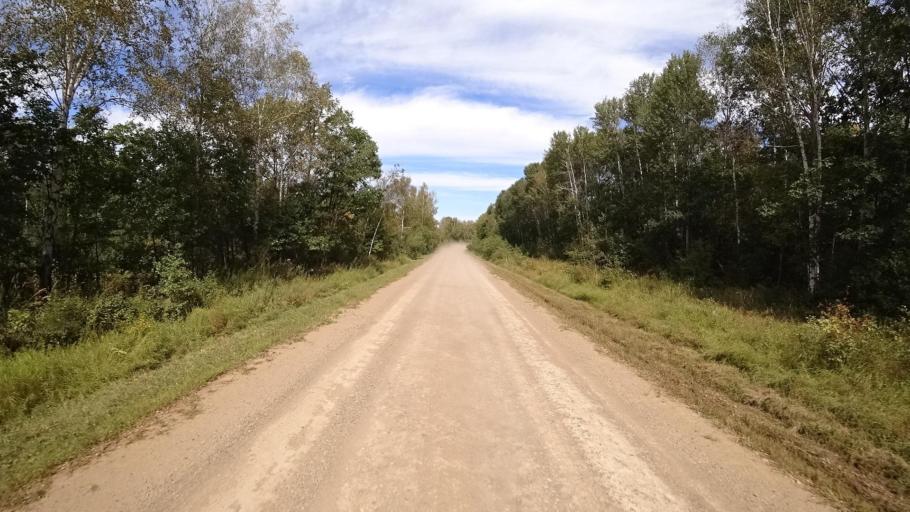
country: RU
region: Primorskiy
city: Yakovlevka
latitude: 44.6929
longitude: 133.6190
